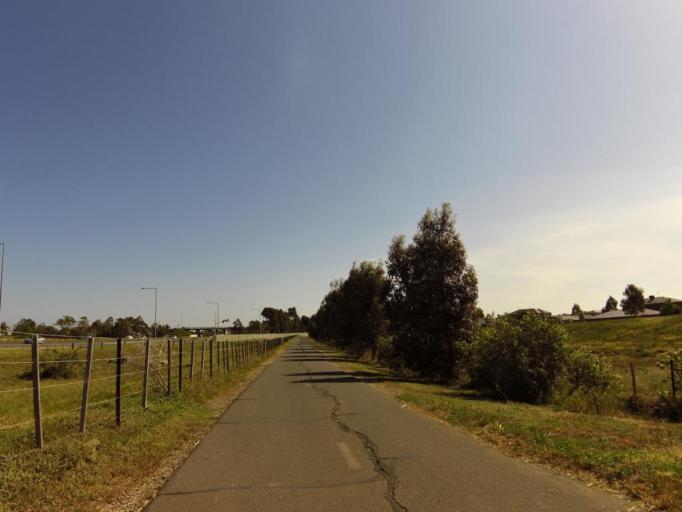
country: AU
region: Victoria
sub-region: Wyndham
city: Werribee
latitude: -37.9100
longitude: 144.6851
